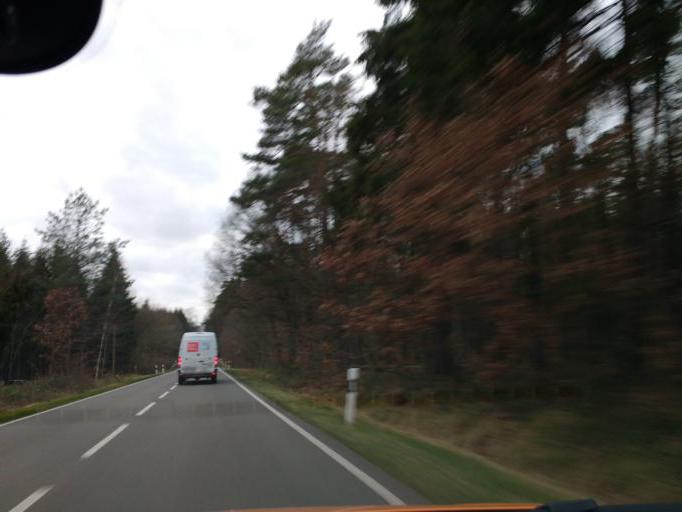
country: DE
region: Brandenburg
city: Protzel
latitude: 52.6443
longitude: 13.9559
